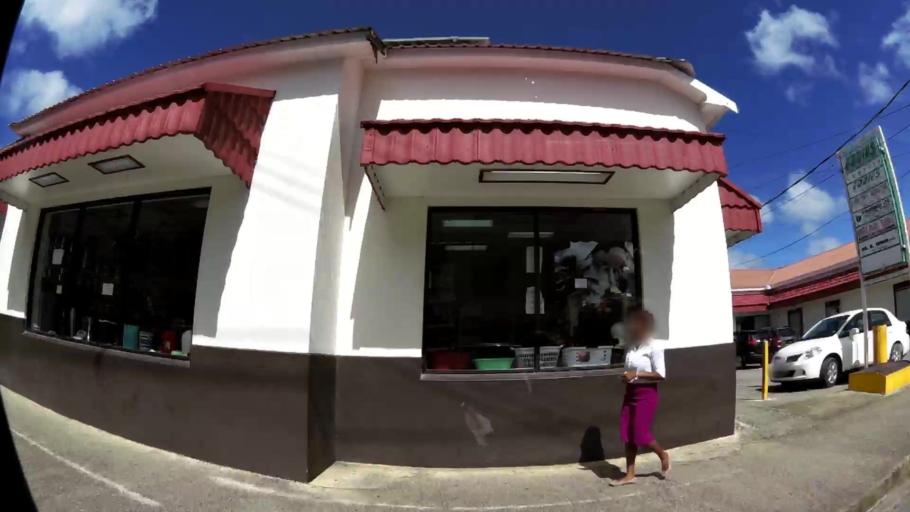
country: BB
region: Saint Peter
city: Speightstown
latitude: 13.2509
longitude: -59.6431
